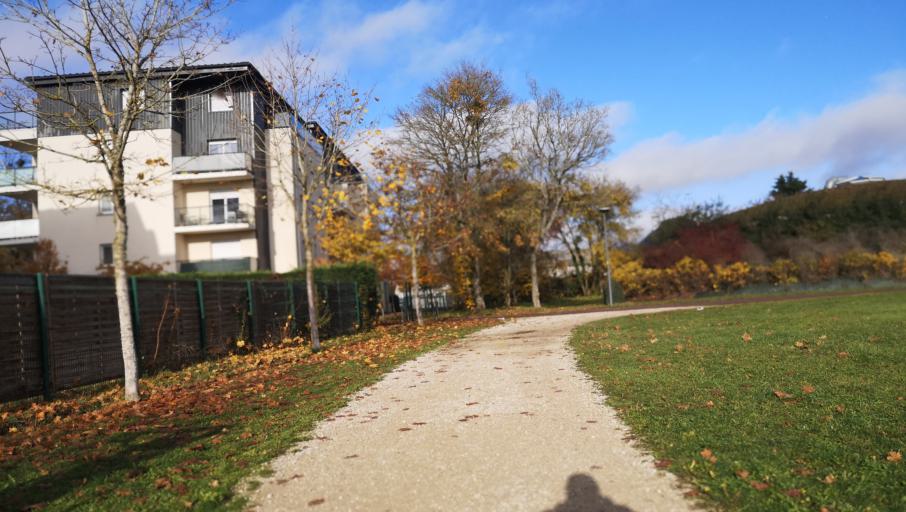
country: FR
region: Centre
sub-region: Departement du Loiret
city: Semoy
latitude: 47.9069
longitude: 1.9482
